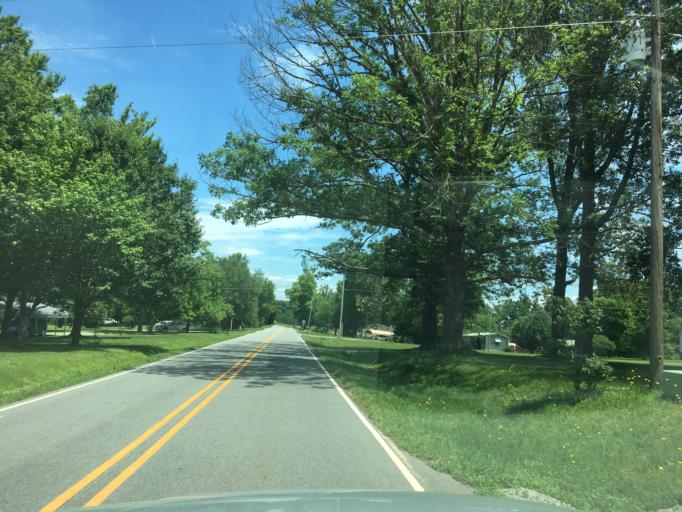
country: US
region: North Carolina
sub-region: Burke County
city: Glen Alpine
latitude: 35.6470
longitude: -81.7880
